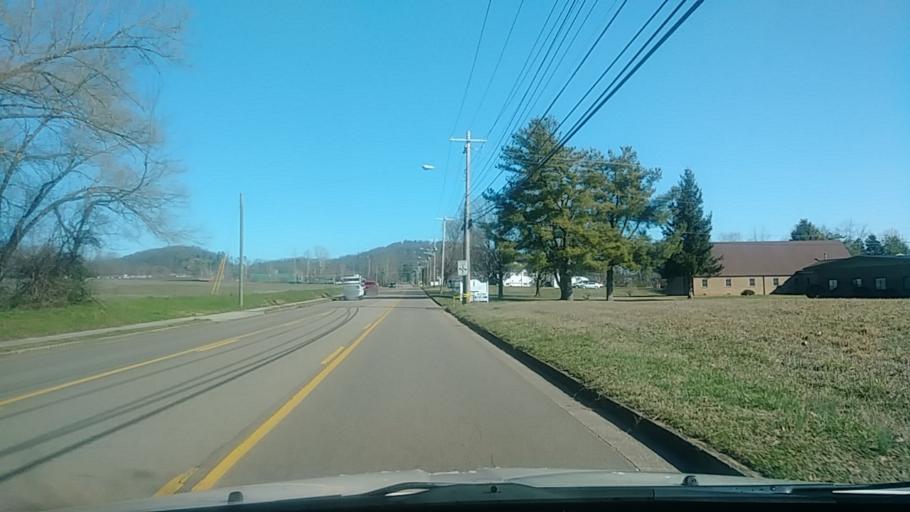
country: US
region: Tennessee
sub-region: Hamblen County
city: Morristown
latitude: 36.2035
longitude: -83.3349
